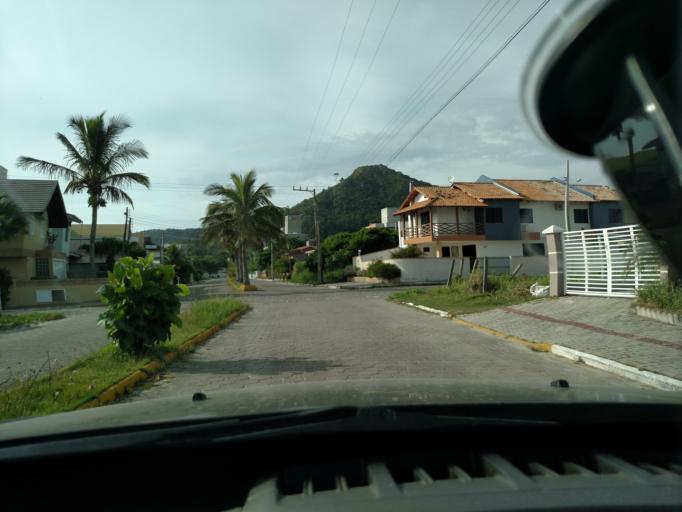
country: BR
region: Santa Catarina
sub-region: Porto Belo
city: Porto Belo
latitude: -27.1945
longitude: -48.4980
